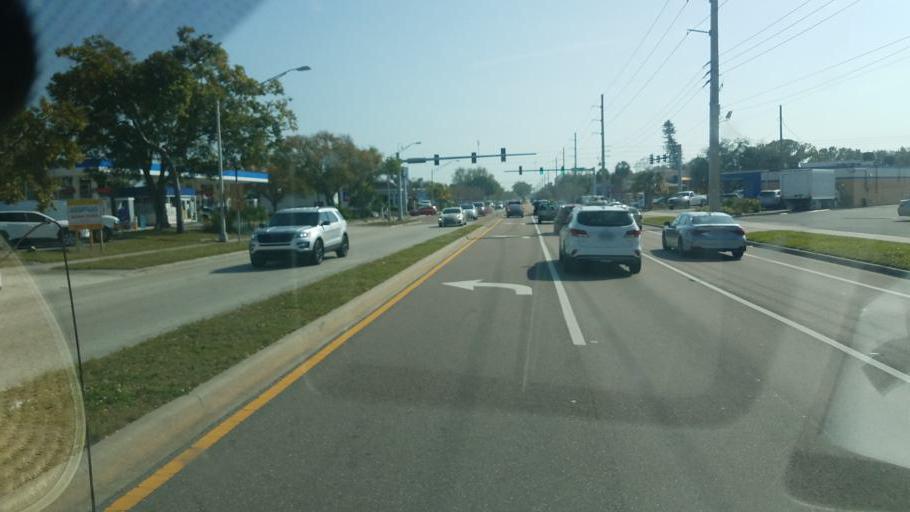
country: US
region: Florida
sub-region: Sarasota County
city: Southgate
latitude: 27.3093
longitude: -82.4976
